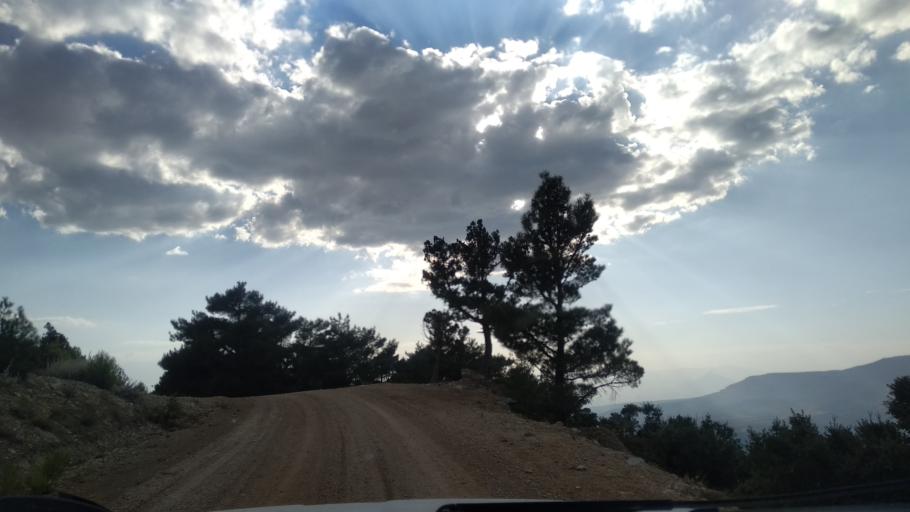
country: TR
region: Mersin
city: Sarikavak
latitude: 36.5976
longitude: 33.6881
